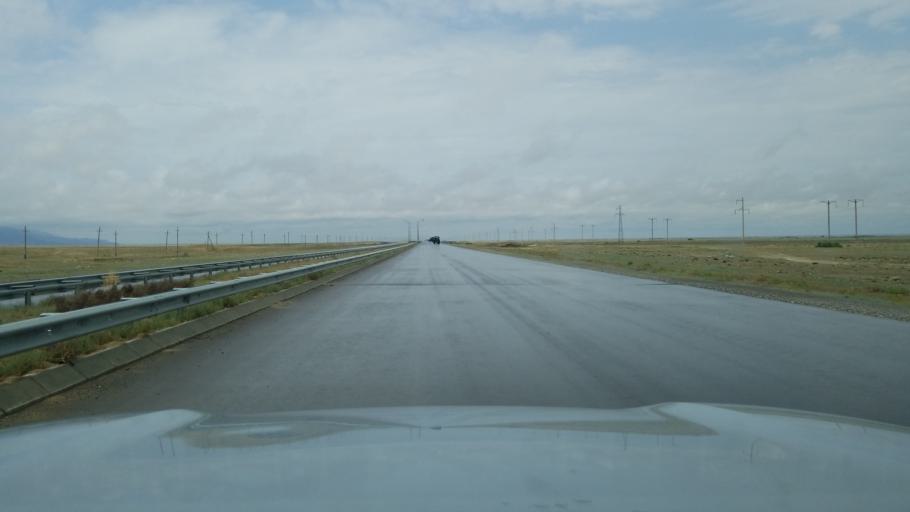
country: TM
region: Balkan
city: Gazanjyk
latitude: 39.1723
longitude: 55.8183
